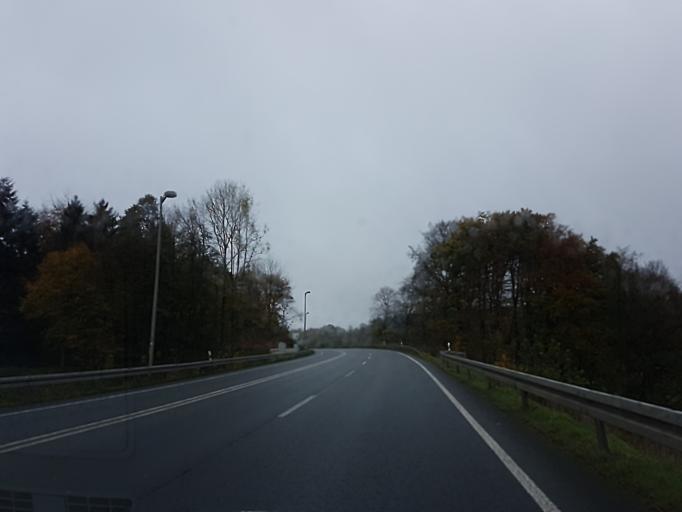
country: DE
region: North Rhine-Westphalia
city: Meinerzhagen
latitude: 51.1045
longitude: 7.6618
